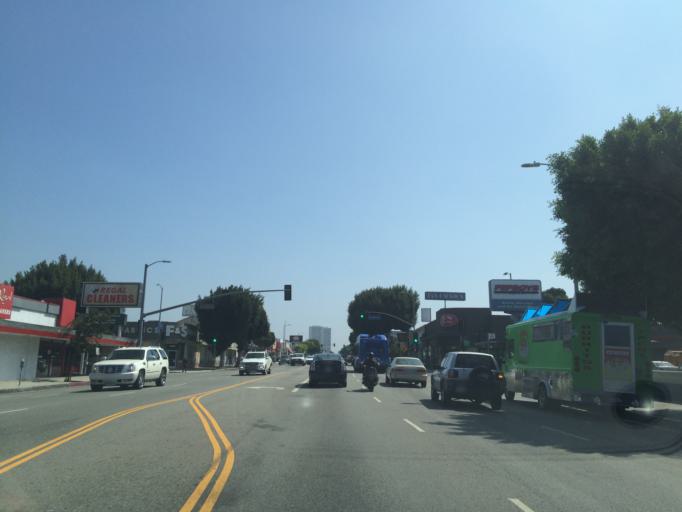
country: US
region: California
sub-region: Los Angeles County
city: Century City
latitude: 34.0426
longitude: -118.4235
